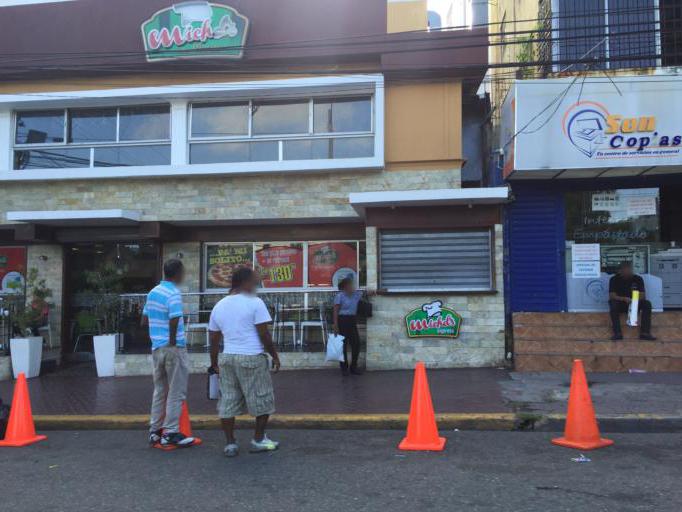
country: DO
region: Nacional
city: La Julia
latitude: 18.4626
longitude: -69.9197
